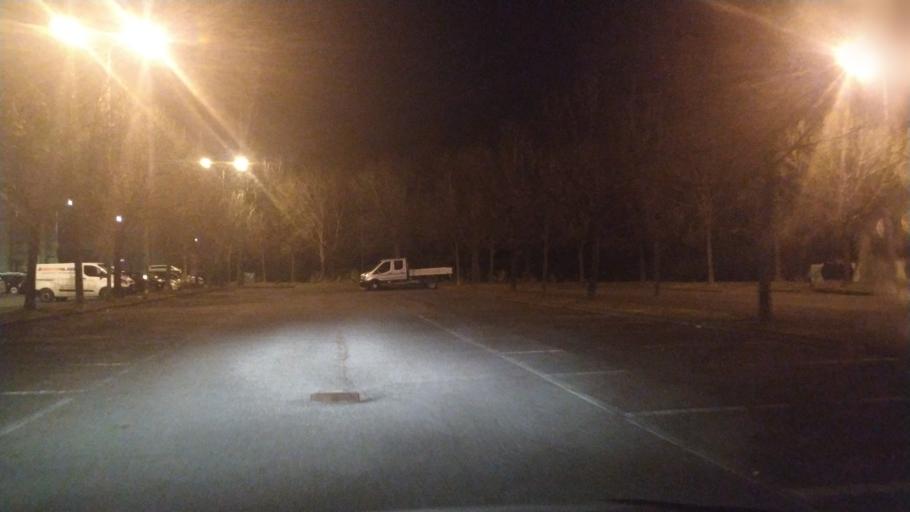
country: IT
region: Piedmont
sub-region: Provincia di Biella
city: Ponderano
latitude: 45.5502
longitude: 8.0634
